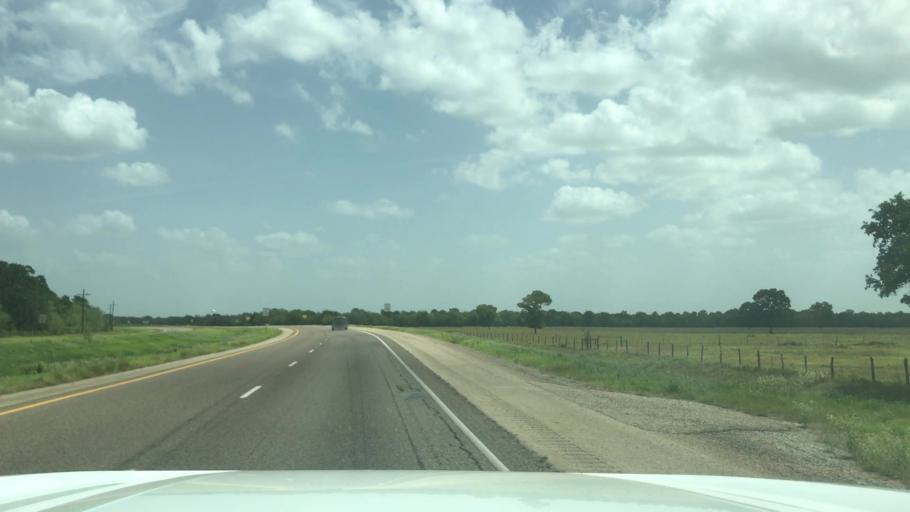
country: US
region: Texas
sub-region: Robertson County
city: Calvert
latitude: 30.9961
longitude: -96.6917
